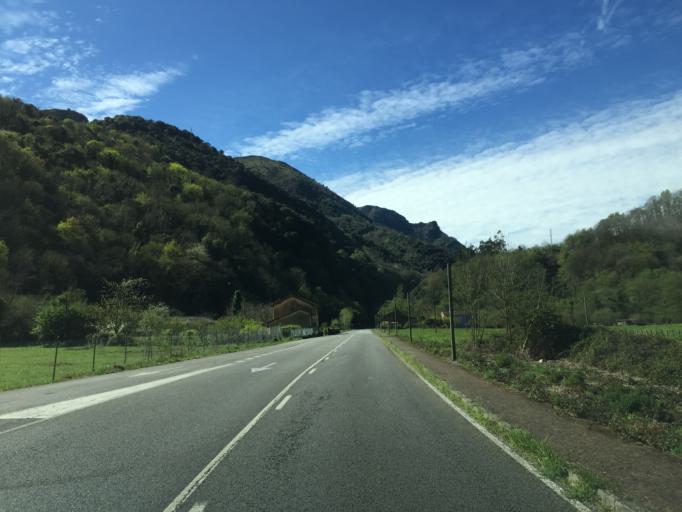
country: ES
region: Asturias
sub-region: Province of Asturias
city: Proaza
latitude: 43.2904
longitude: -5.9825
